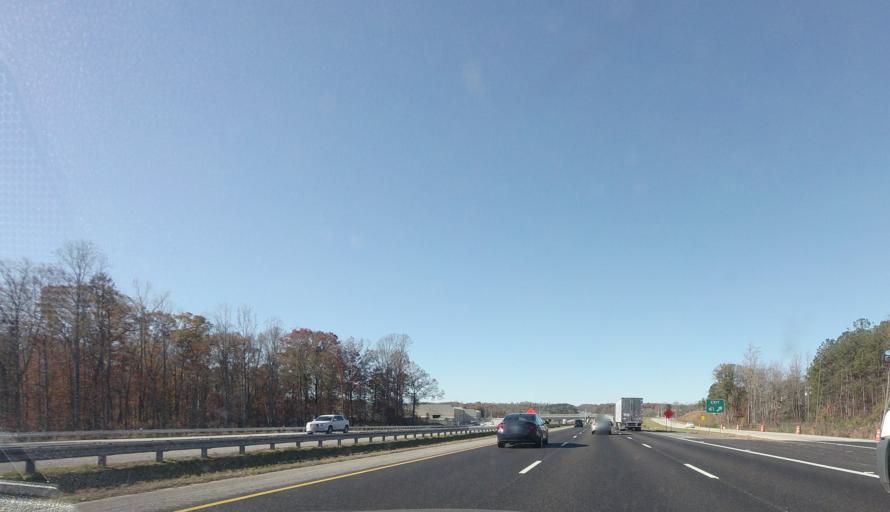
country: US
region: Georgia
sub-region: Douglas County
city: Lithia Springs
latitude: 33.7699
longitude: -84.6465
